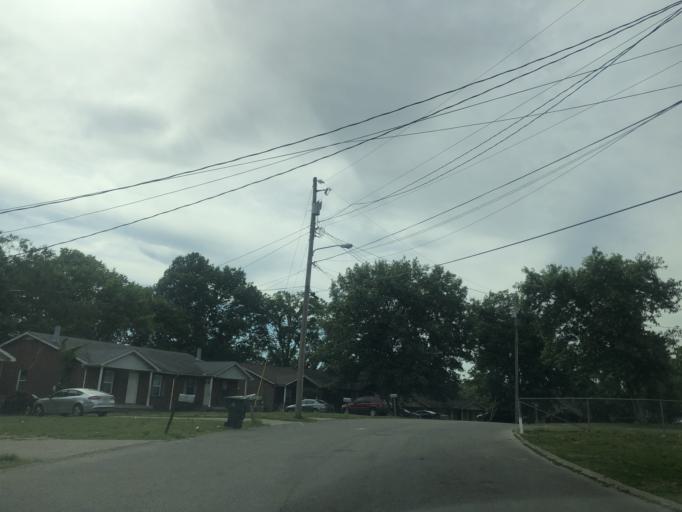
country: US
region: Tennessee
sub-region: Davidson County
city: Nashville
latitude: 36.2230
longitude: -86.8170
